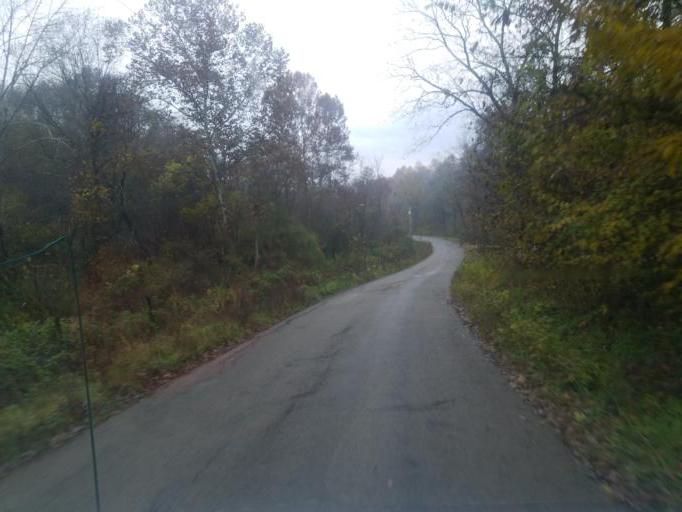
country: US
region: Ohio
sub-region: Athens County
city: Glouster
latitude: 39.5295
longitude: -81.9452
